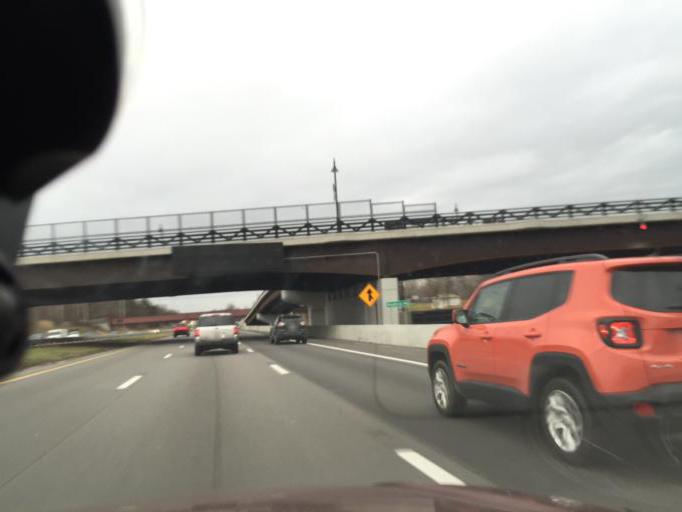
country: US
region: New York
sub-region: Monroe County
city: Rochester
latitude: 43.1158
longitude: -77.6321
